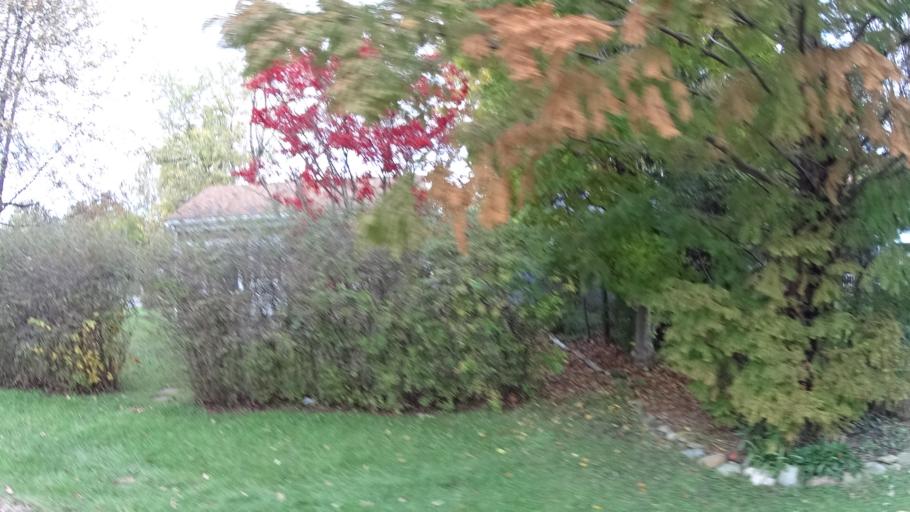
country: US
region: Ohio
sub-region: Lorain County
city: Sheffield
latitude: 41.4215
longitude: -82.1229
